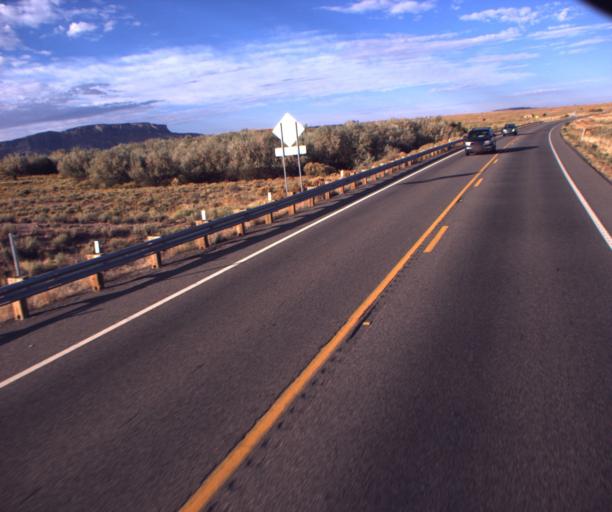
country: US
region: New Mexico
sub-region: San Juan County
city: Shiprock
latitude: 36.9263
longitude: -109.1740
